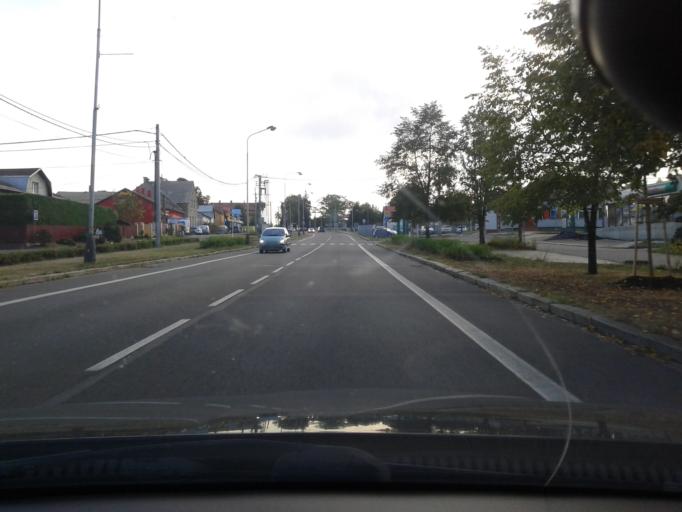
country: CZ
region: Moravskoslezsky
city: Orlova
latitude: 49.8509
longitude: 18.4185
